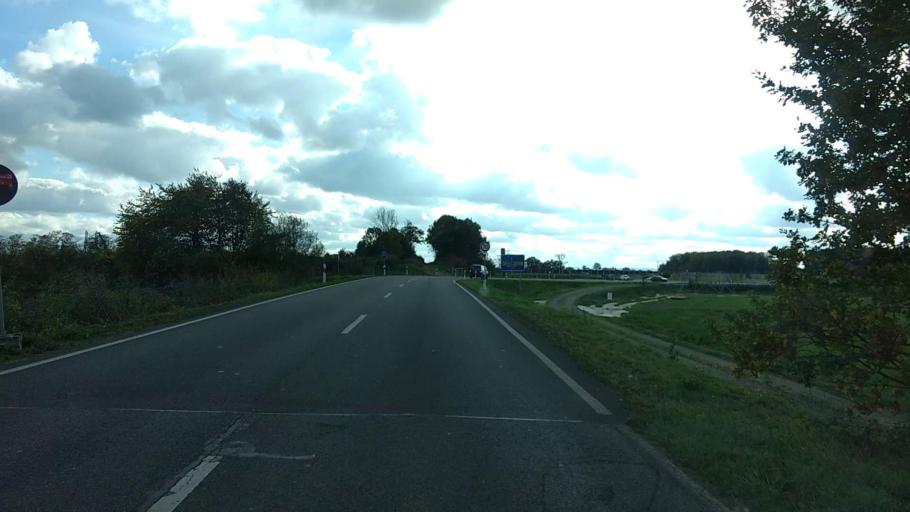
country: DE
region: North Rhine-Westphalia
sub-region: Regierungsbezirk Koln
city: Bergheim
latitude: 50.8967
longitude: 6.6424
